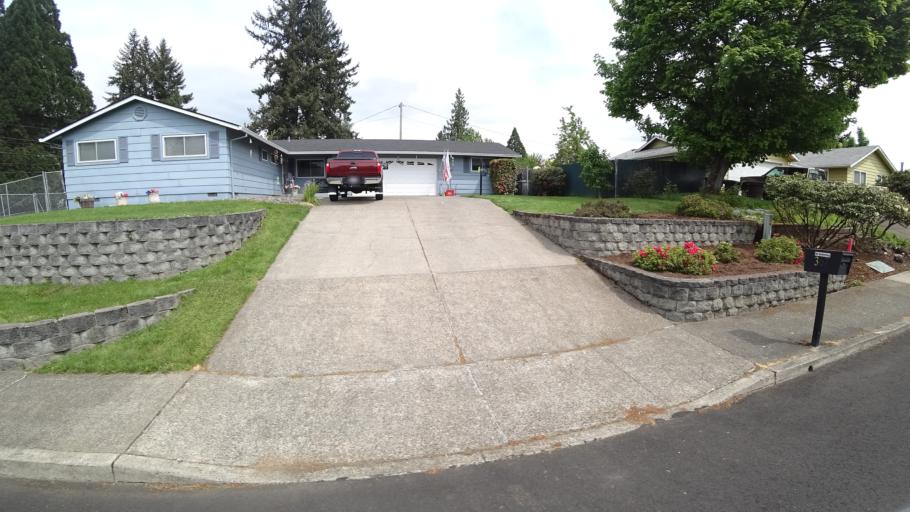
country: US
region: Oregon
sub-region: Washington County
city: Hillsboro
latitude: 45.5309
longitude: -122.9930
